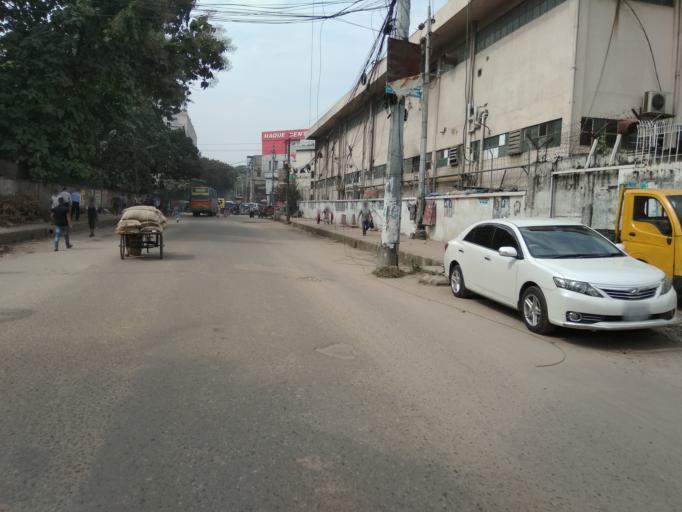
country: BD
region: Dhaka
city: Paltan
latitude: 23.7660
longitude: 90.4013
